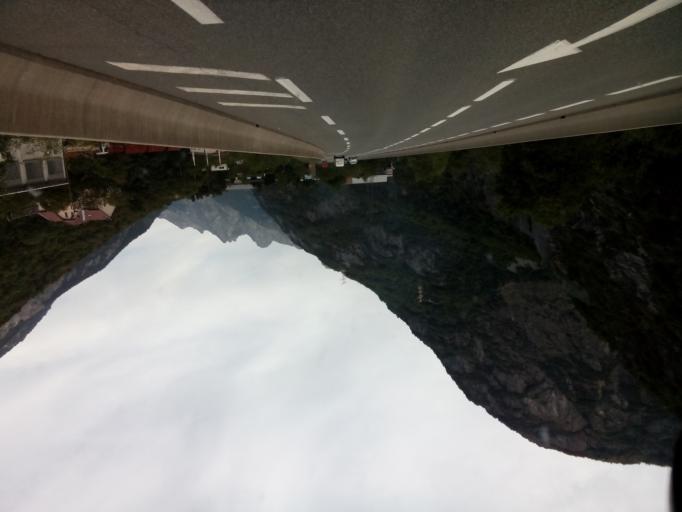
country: FR
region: Rhone-Alpes
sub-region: Departement de l'Isere
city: Vaulnaveys-le-Bas
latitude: 45.0696
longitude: 5.8704
